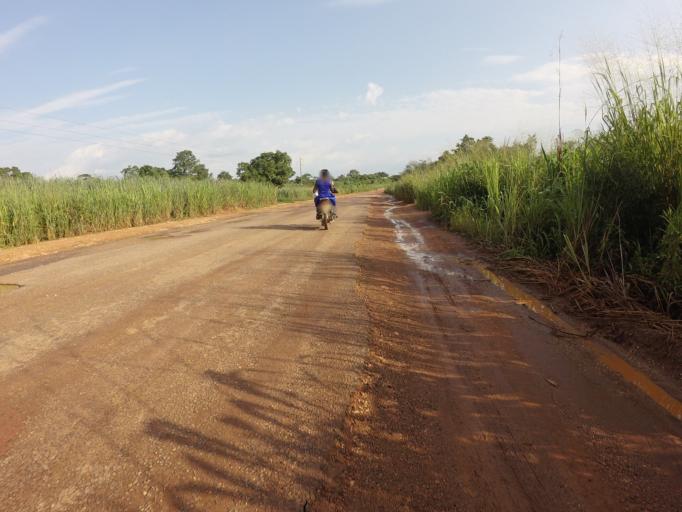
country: GH
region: Volta
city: Hohoe
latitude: 7.0871
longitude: 0.4448
